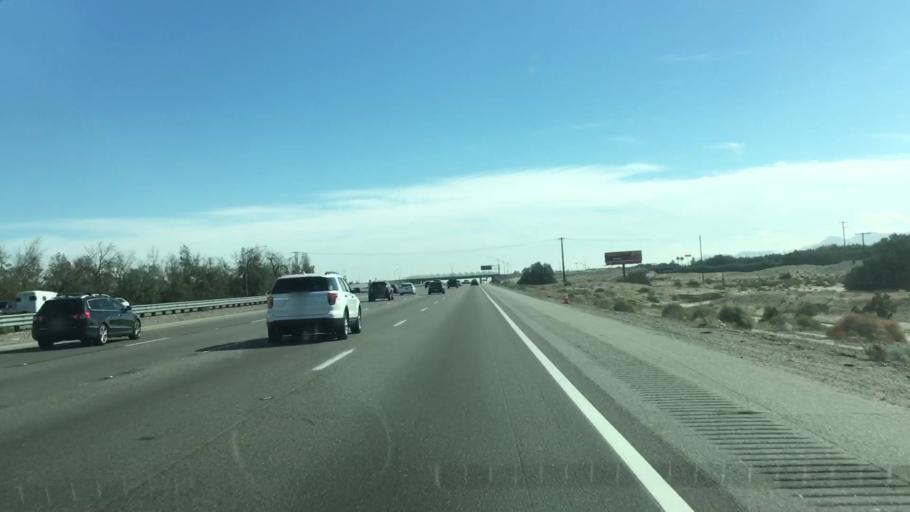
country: US
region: California
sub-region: Riverside County
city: Cathedral City
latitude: 33.8534
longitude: -116.4656
